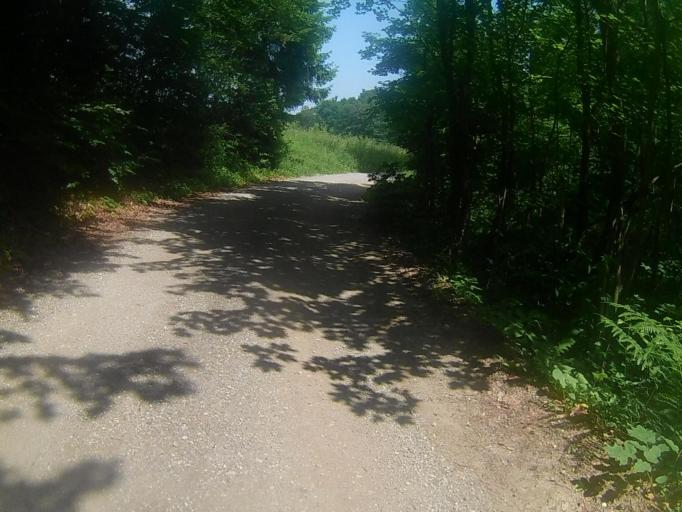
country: SI
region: Maribor
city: Bresternica
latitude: 46.5929
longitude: 15.5867
